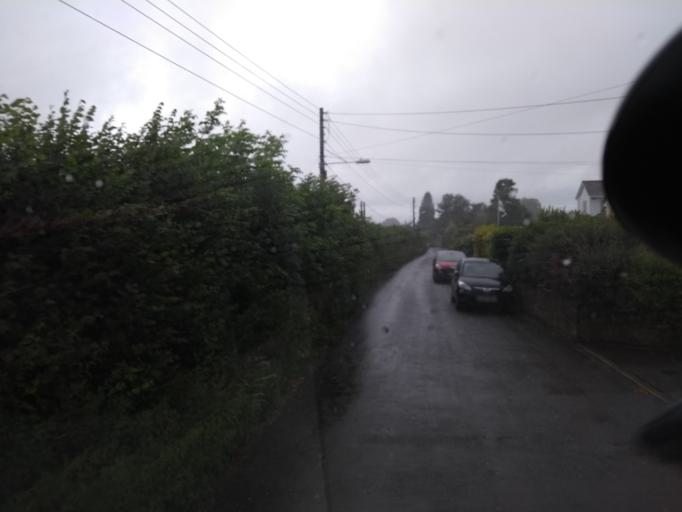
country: GB
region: England
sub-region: Somerset
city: Crewkerne
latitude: 50.8793
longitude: -2.8012
